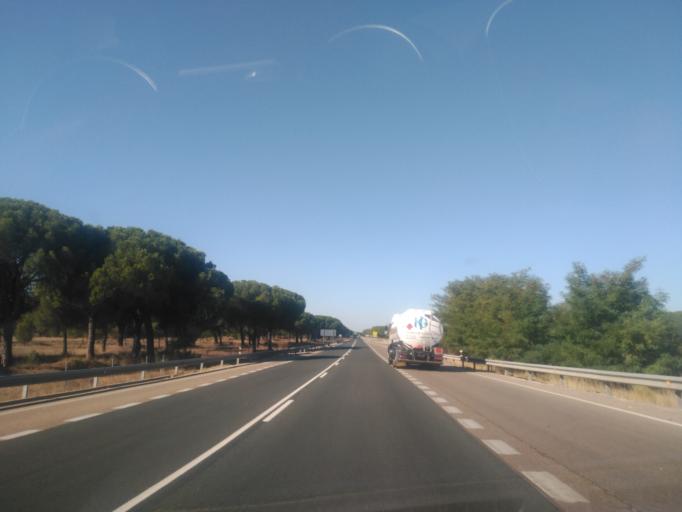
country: ES
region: Castille and Leon
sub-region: Provincia de Valladolid
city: Quintanilla de Onesimo
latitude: 41.6211
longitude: -4.3815
